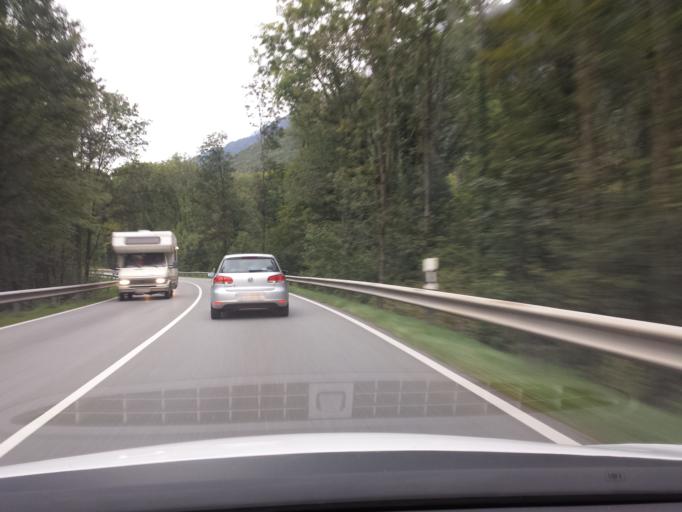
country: DE
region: Bavaria
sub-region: Upper Bavaria
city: Bad Reichenhall
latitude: 47.7405
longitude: 12.8914
